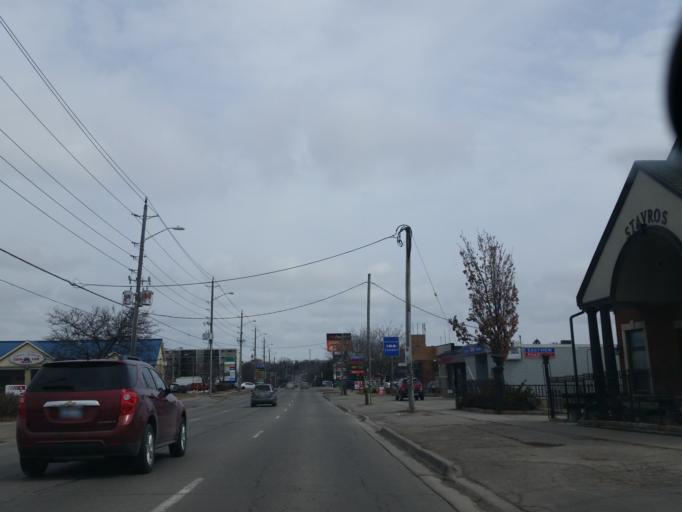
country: CA
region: Ontario
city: Oshawa
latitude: 43.9022
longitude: -78.8433
